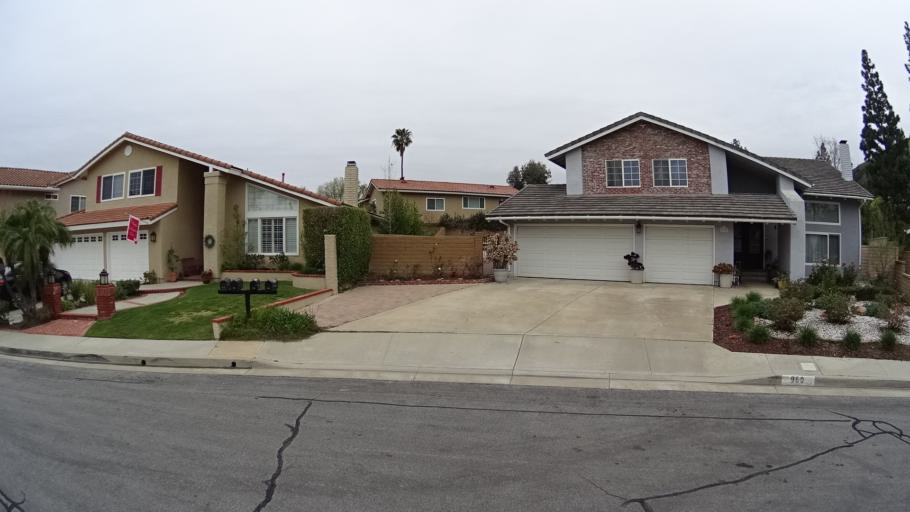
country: US
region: California
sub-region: Orange County
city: Villa Park
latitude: 33.8418
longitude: -117.7435
